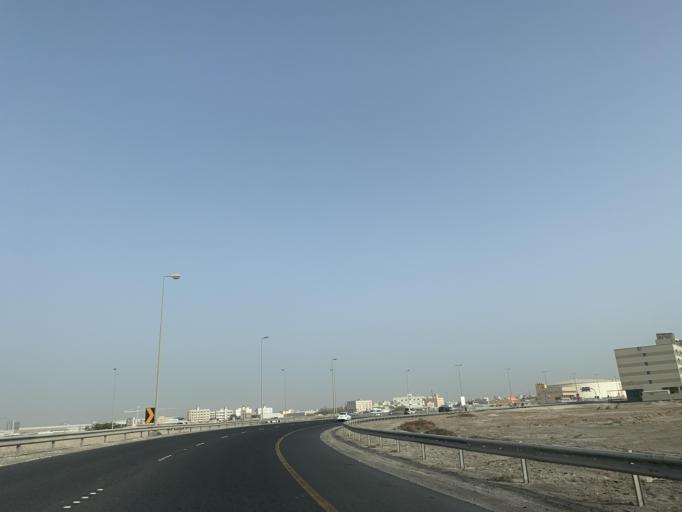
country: BH
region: Northern
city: Madinat `Isa
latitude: 26.1916
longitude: 50.5167
